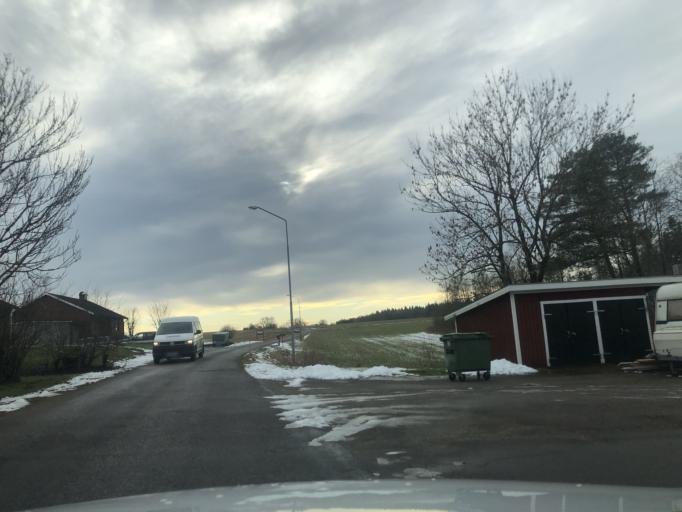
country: SE
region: Vaestra Goetaland
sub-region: Ulricehamns Kommun
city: Ulricehamn
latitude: 57.8187
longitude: 13.5309
